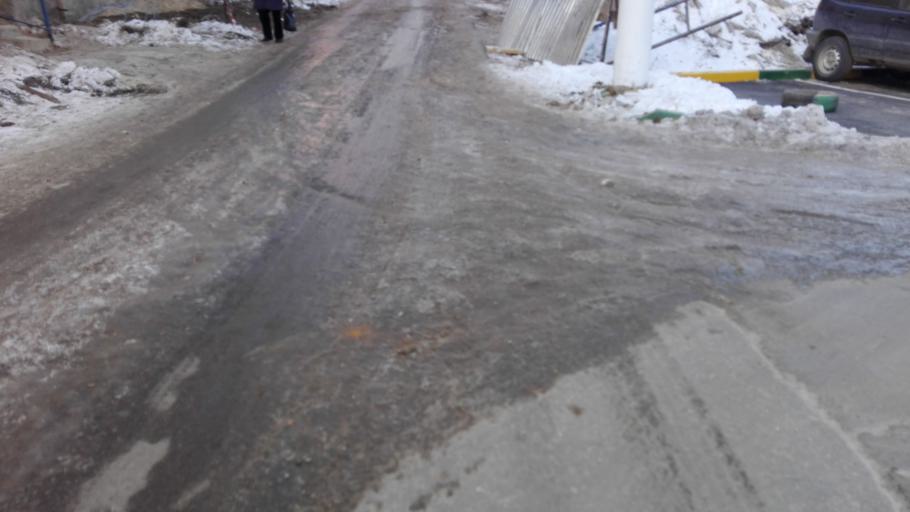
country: RU
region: Tula
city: Kosaya Gora
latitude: 54.1171
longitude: 37.5398
